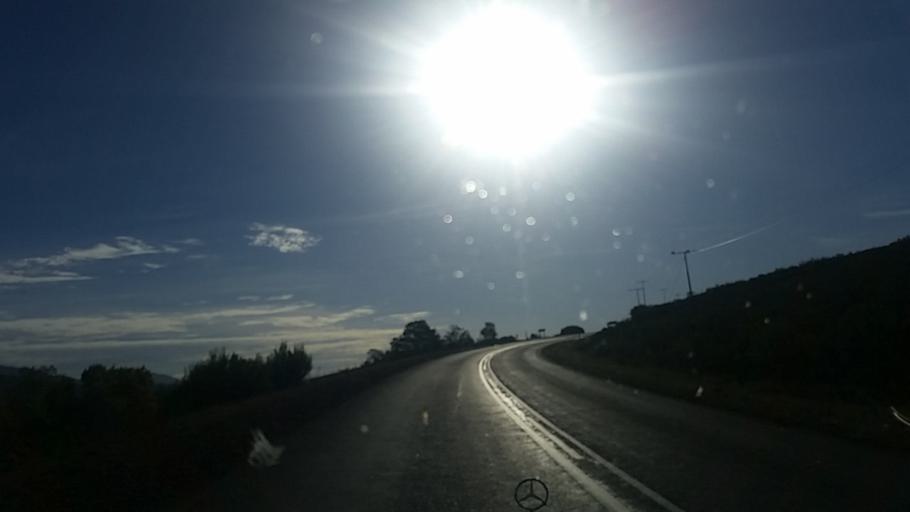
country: ZA
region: Western Cape
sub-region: Eden District Municipality
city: Knysna
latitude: -33.7602
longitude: 22.9552
